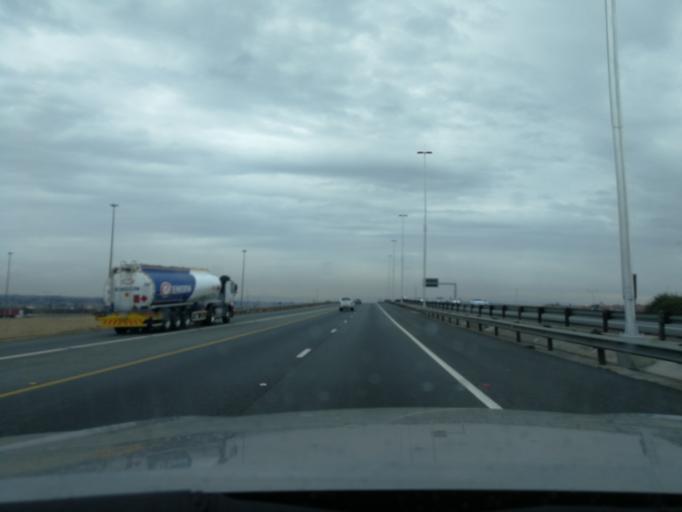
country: ZA
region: Gauteng
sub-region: Ekurhuleni Metropolitan Municipality
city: Germiston
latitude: -26.2890
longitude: 28.1540
